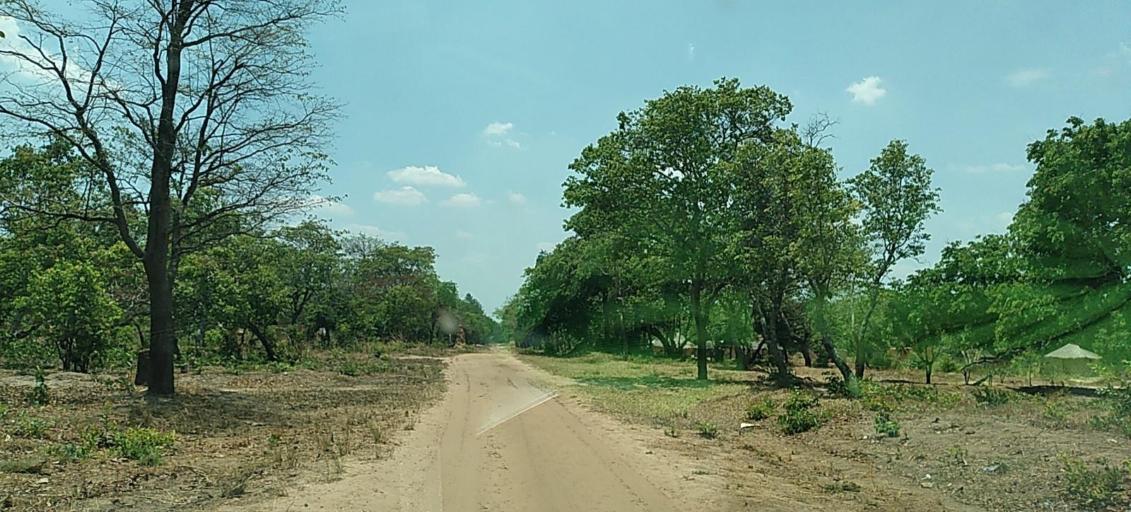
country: CD
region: Katanga
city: Kolwezi
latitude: -11.3799
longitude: 25.2176
